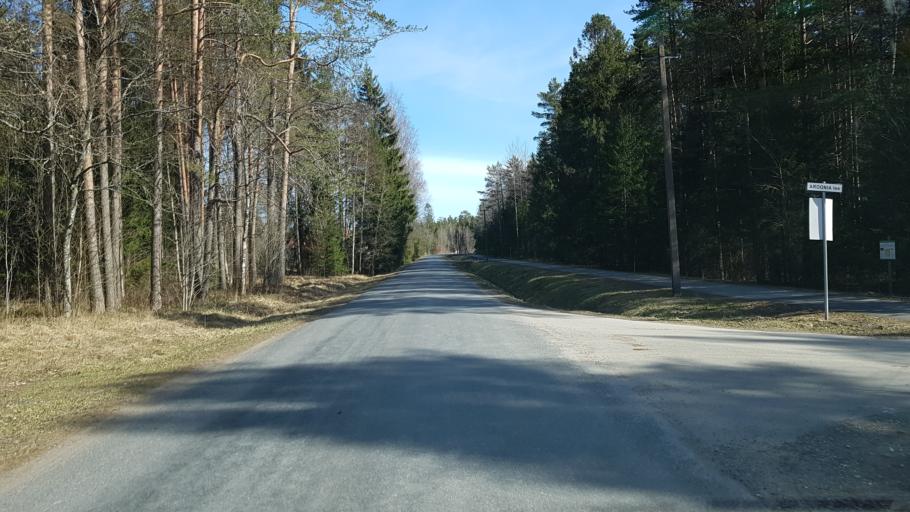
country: EE
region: Harju
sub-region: Saku vald
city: Saku
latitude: 59.2616
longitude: 24.6591
